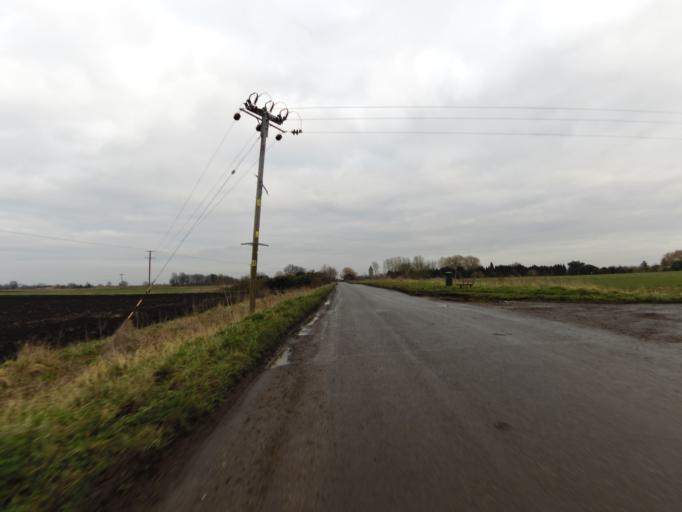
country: GB
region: England
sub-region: Cambridgeshire
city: Waterbeach
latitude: 52.2699
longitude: 0.2045
